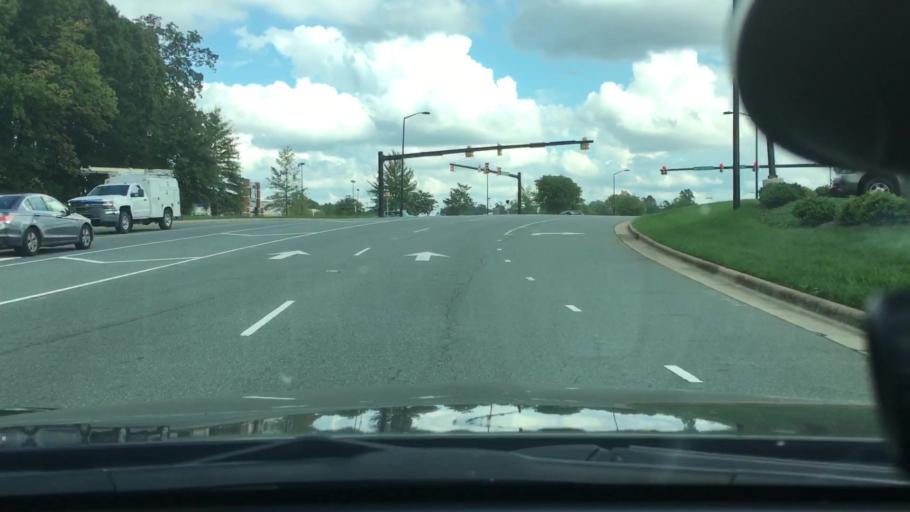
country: US
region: North Carolina
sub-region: Alamance County
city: Elon
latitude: 36.0691
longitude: -79.5172
